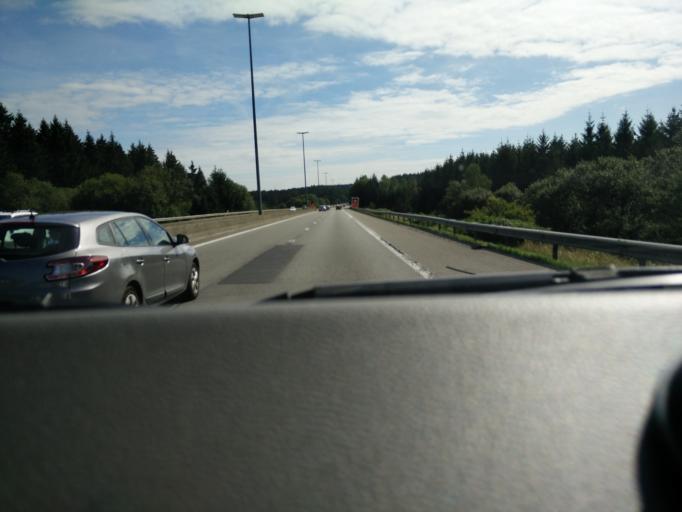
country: BE
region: Wallonia
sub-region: Province du Luxembourg
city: Bertrix
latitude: 49.9105
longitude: 5.2909
